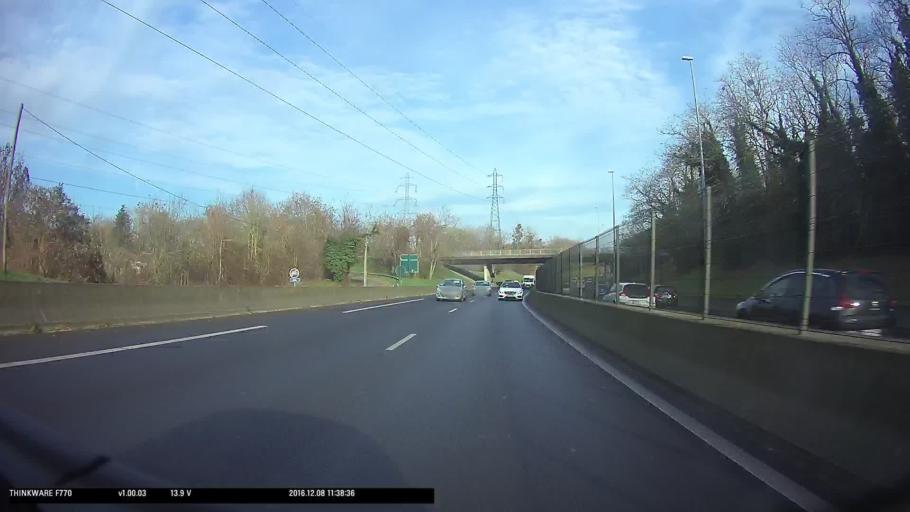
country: FR
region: Ile-de-France
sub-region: Departement du Val-d'Oise
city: Cergy-Pontoise
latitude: 49.0560
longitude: 2.0814
